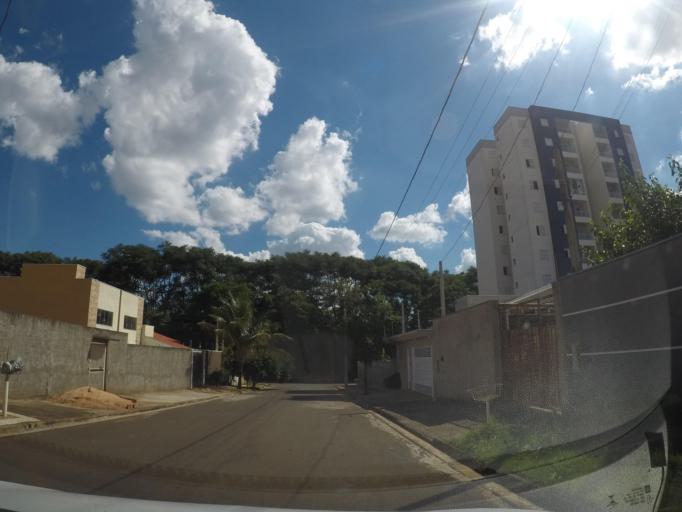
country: BR
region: Sao Paulo
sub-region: Sumare
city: Sumare
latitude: -22.8368
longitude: -47.2729
